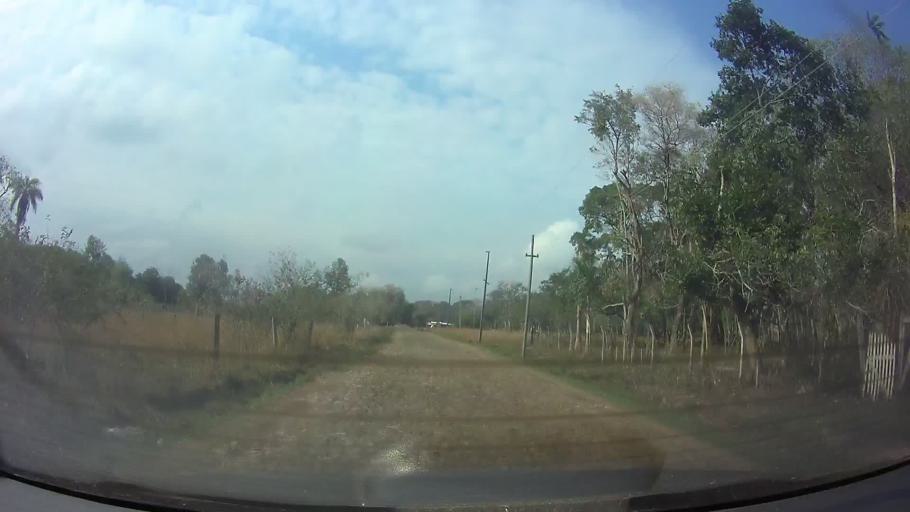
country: PY
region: Cordillera
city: Arroyos y Esteros
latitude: -25.0022
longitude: -57.1969
